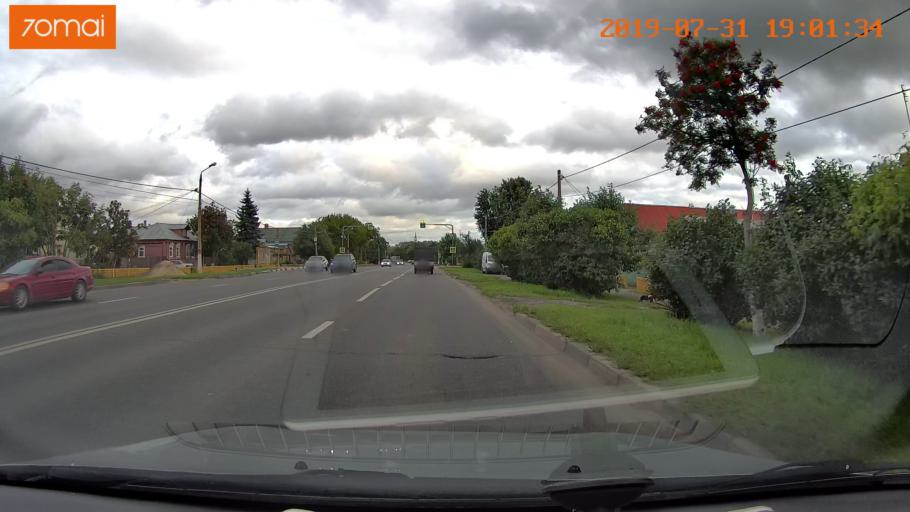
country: RU
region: Moskovskaya
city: Raduzhnyy
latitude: 55.1256
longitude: 38.7291
